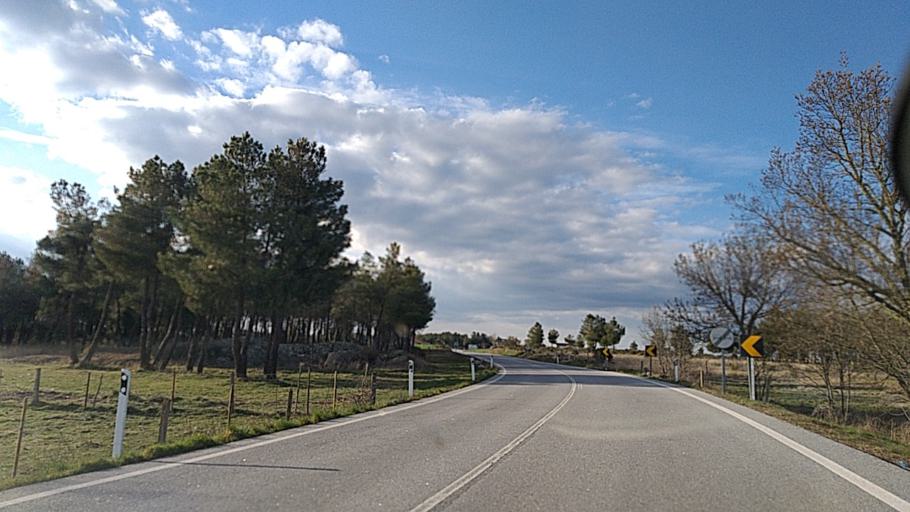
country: ES
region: Castille and Leon
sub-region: Provincia de Salamanca
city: Aldea del Obispo
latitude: 40.6700
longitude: -6.8595
